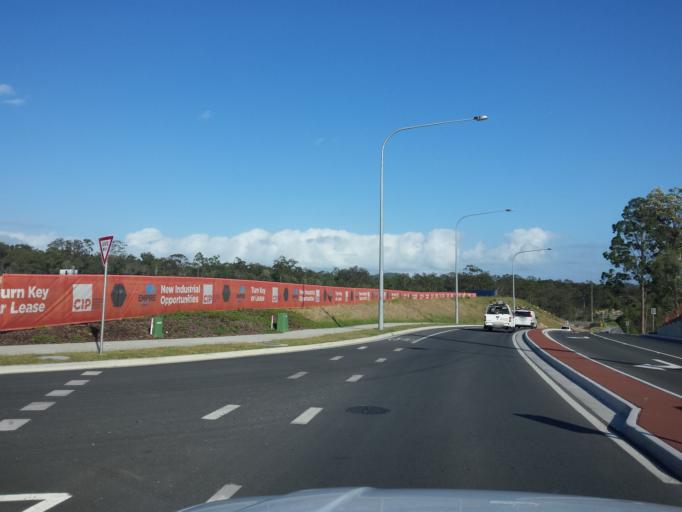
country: AU
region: Queensland
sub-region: Logan
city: Windaroo
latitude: -27.7638
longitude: 153.2152
